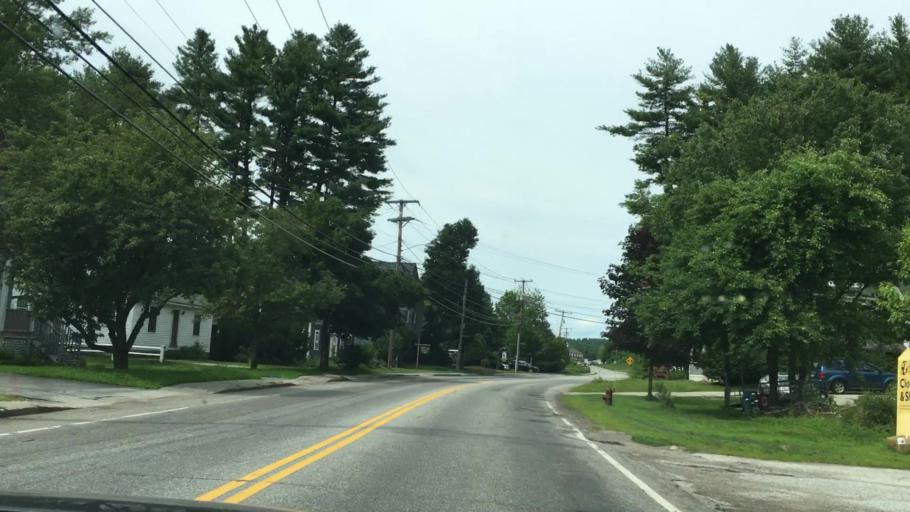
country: US
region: New Hampshire
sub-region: Hillsborough County
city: Peterborough
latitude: 42.8839
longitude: -71.9463
